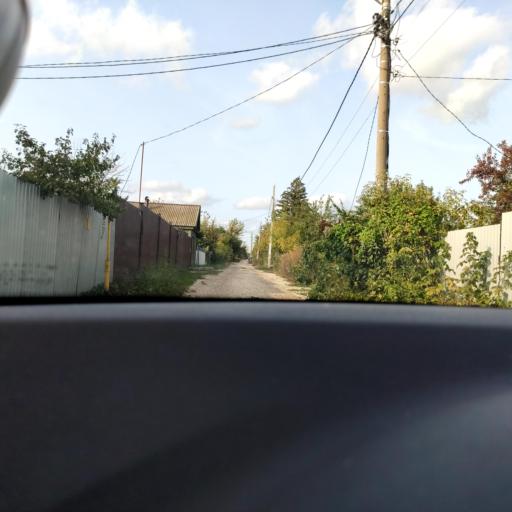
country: RU
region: Samara
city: Petra-Dubrava
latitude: 53.2774
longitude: 50.2966
